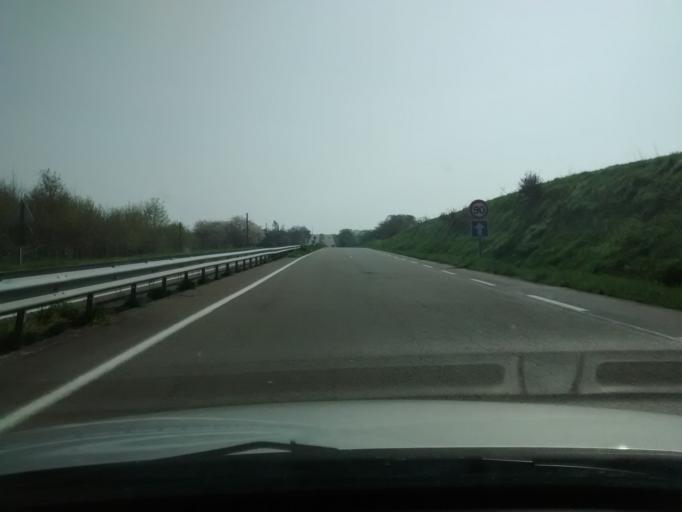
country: FR
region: Pays de la Loire
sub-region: Departement de la Mayenne
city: Argentre
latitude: 48.0667
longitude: -0.6542
